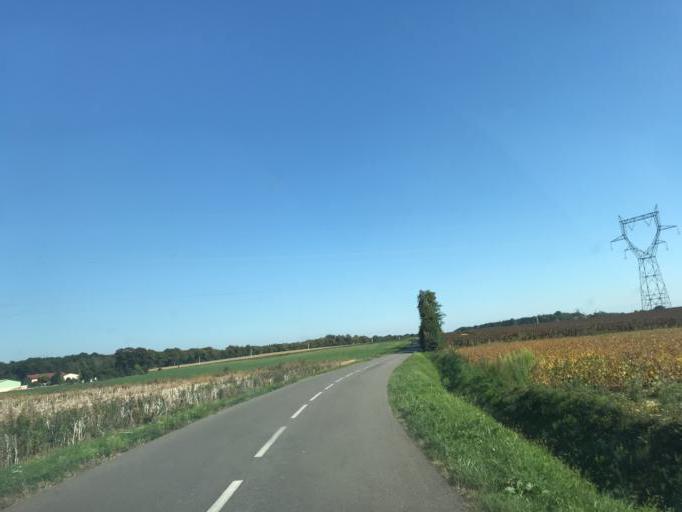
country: FR
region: Rhone-Alpes
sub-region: Departement de l'Ain
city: Beynost
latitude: 45.8657
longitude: 4.9940
